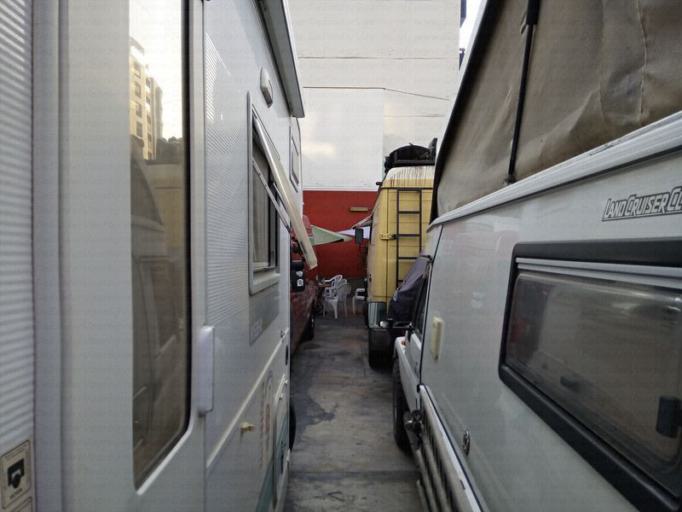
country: PE
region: Ica
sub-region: Provincia de Pisco
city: Paracas
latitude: -13.8296
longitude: -76.2468
